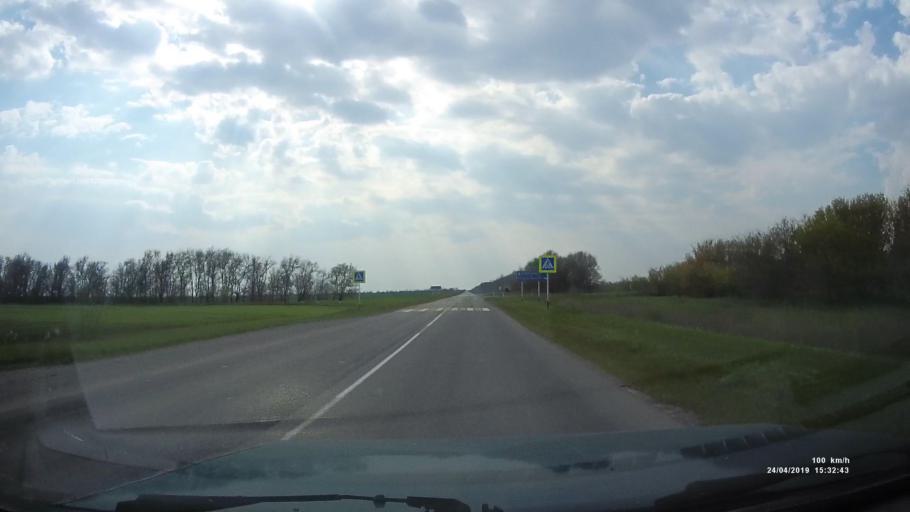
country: RU
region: Rostov
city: Remontnoye
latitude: 46.5996
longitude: 42.9541
